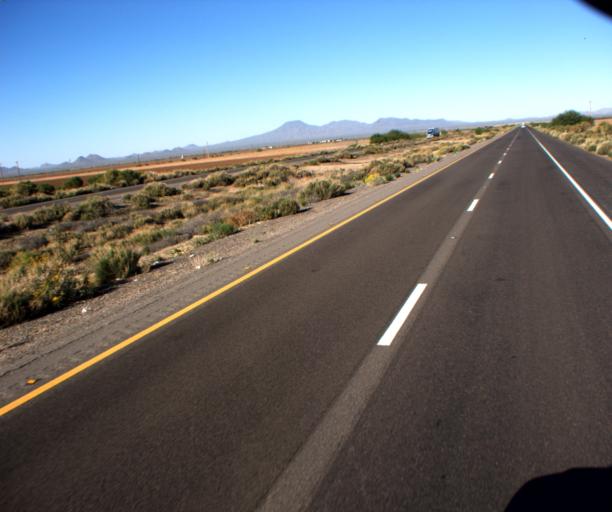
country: US
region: Arizona
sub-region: Pinal County
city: Casa Grande
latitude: 32.8283
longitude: -111.8831
